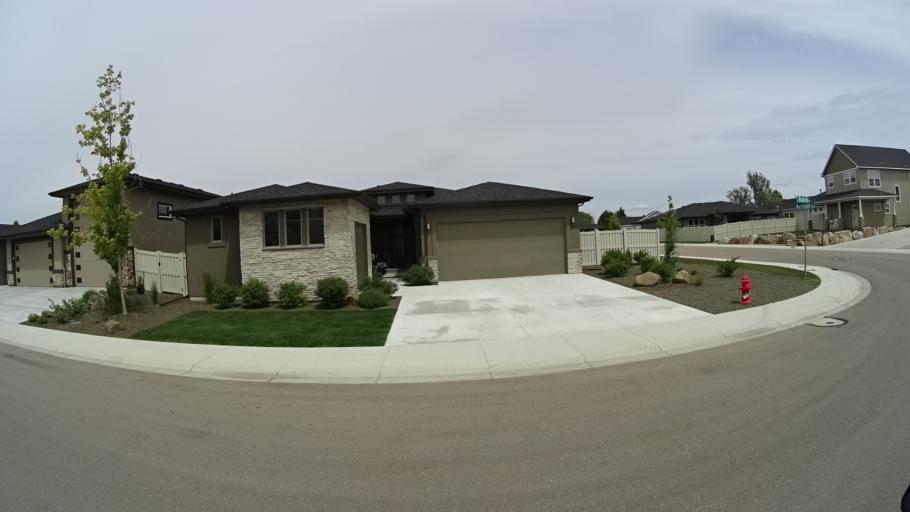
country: US
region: Idaho
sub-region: Ada County
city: Meridian
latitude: 43.5652
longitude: -116.3504
